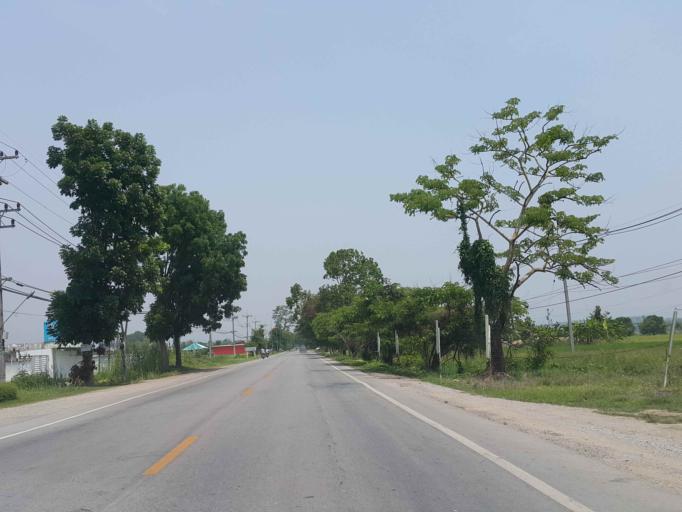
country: TH
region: Chiang Mai
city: Mae Taeng
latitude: 19.0437
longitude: 98.9669
